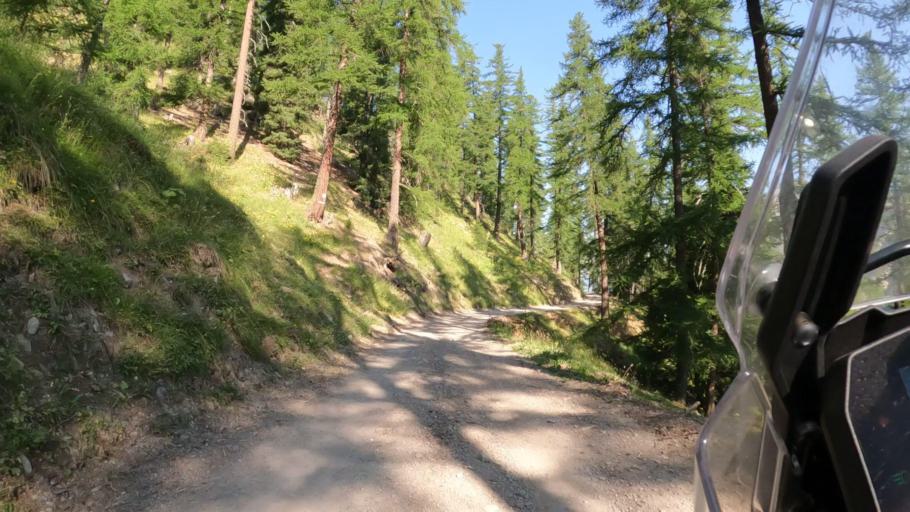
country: FR
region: Provence-Alpes-Cote d'Azur
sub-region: Departement des Hautes-Alpes
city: Guillestre
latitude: 44.5887
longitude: 6.6080
